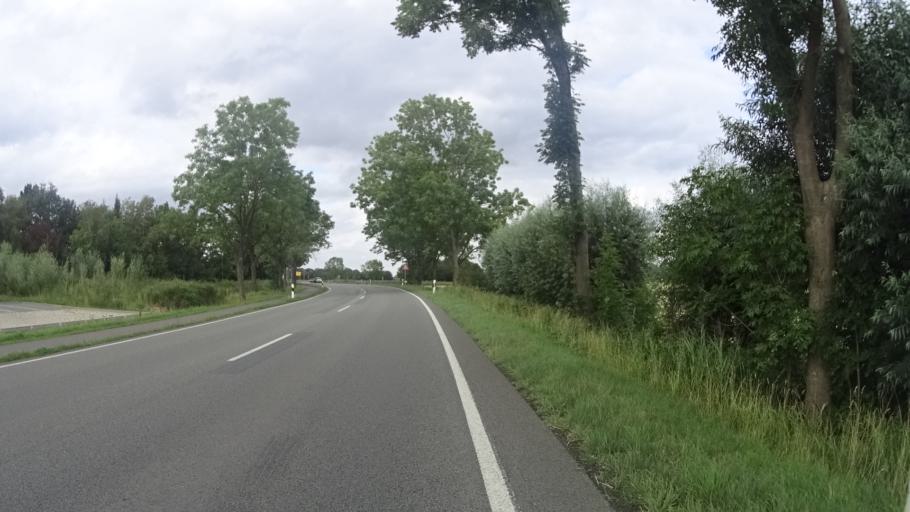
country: DE
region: Lower Saxony
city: Wischhafen
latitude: 53.7811
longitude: 9.3255
